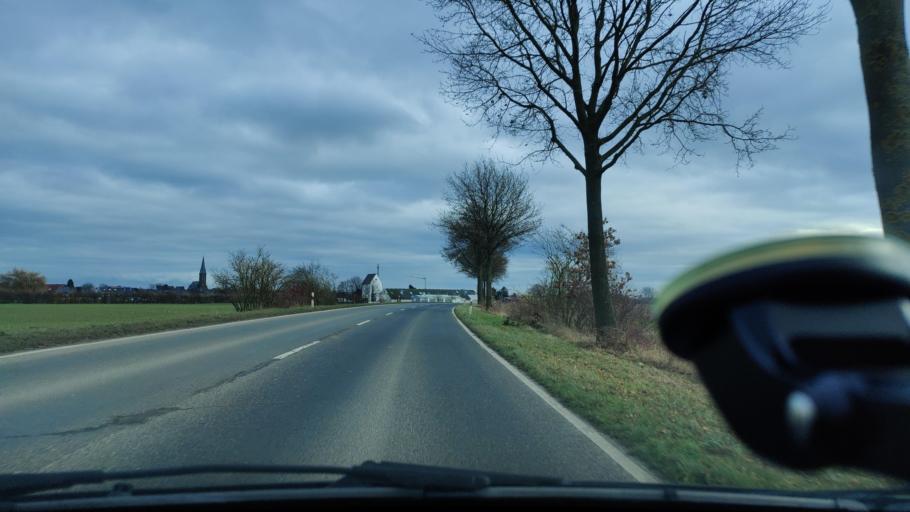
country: DE
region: North Rhine-Westphalia
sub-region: Regierungsbezirk Koln
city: Titz
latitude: 51.0071
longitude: 6.4129
